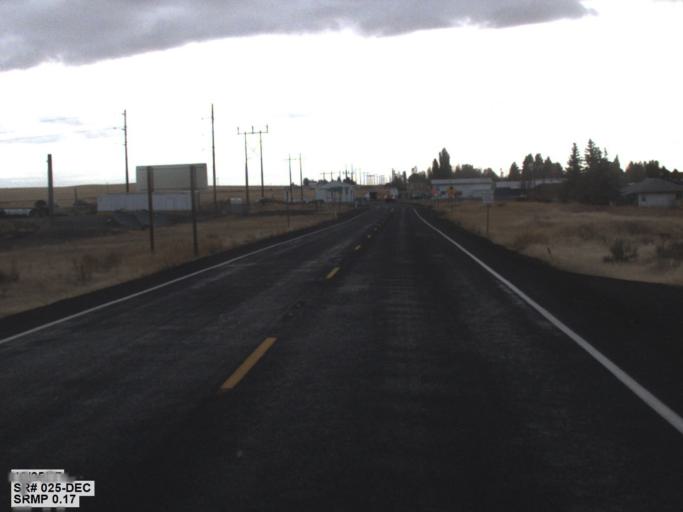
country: US
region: Washington
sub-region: Lincoln County
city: Davenport
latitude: 47.6574
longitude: -118.1410
